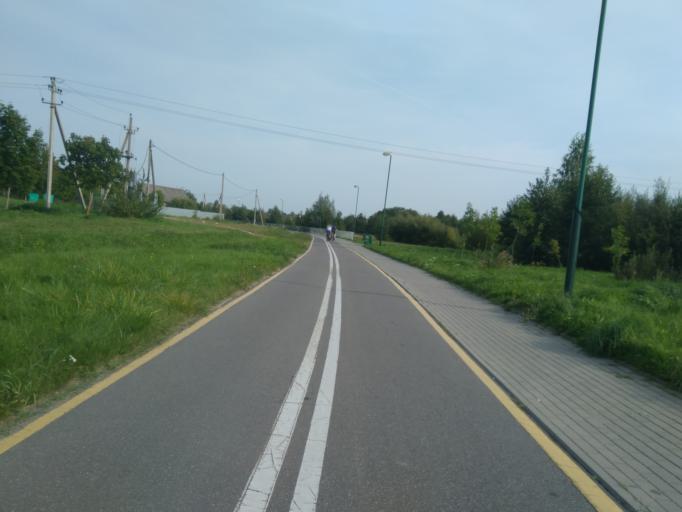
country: BY
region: Minsk
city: Minsk
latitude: 53.8492
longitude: 27.5888
